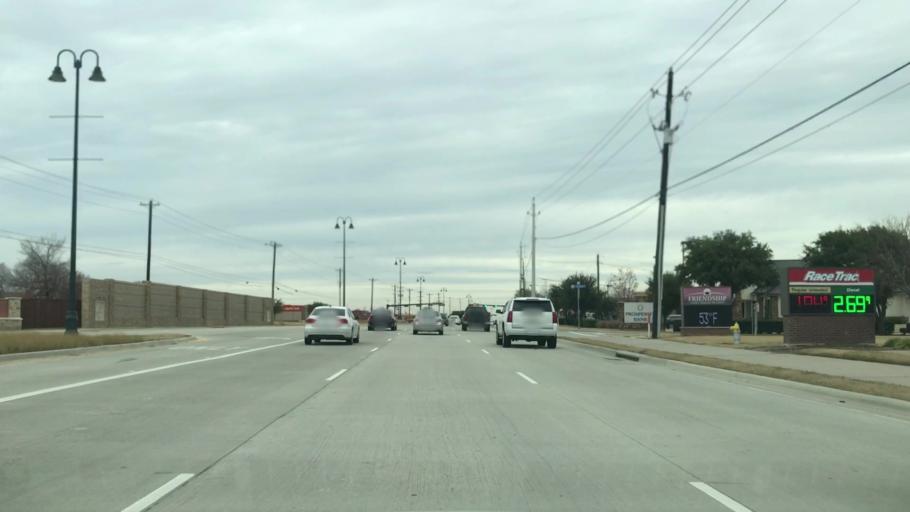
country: US
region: Texas
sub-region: Denton County
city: The Colony
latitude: 33.0755
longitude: -96.8926
